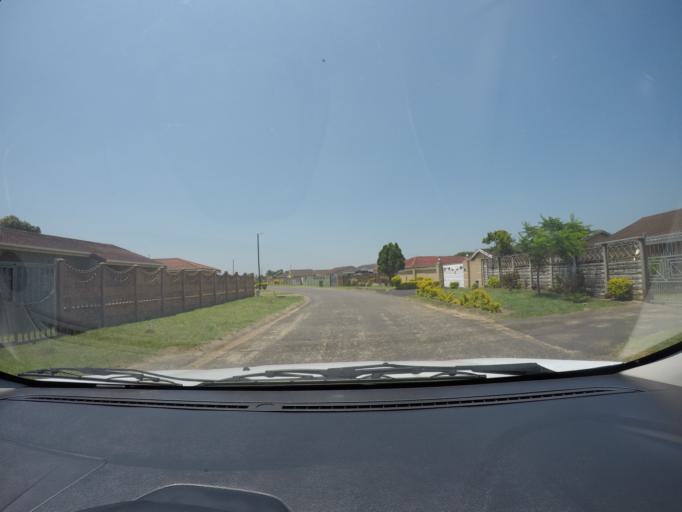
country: ZA
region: KwaZulu-Natal
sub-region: uThungulu District Municipality
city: eSikhawini
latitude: -28.8897
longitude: 31.8842
